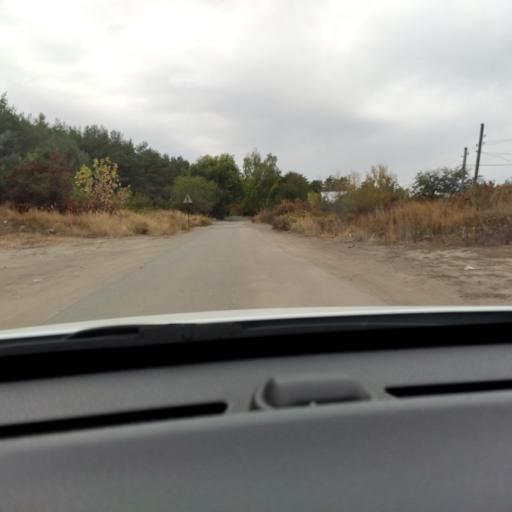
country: RU
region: Voronezj
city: Maslovka
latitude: 51.6021
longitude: 39.2771
